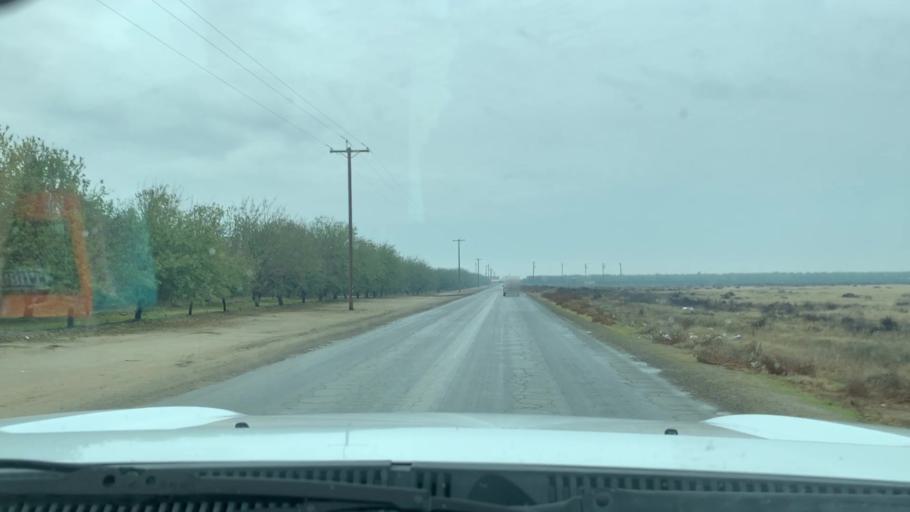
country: US
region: California
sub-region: Kern County
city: Delano
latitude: 35.7612
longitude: -119.3533
